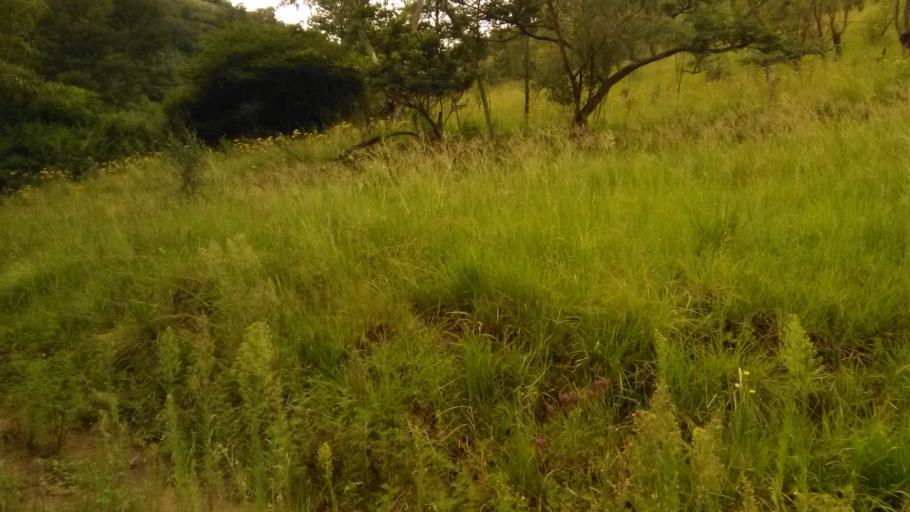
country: ZA
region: KwaZulu-Natal
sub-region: eThekwini Metropolitan Municipality
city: Mpumalanga
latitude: -29.7439
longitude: 30.6661
